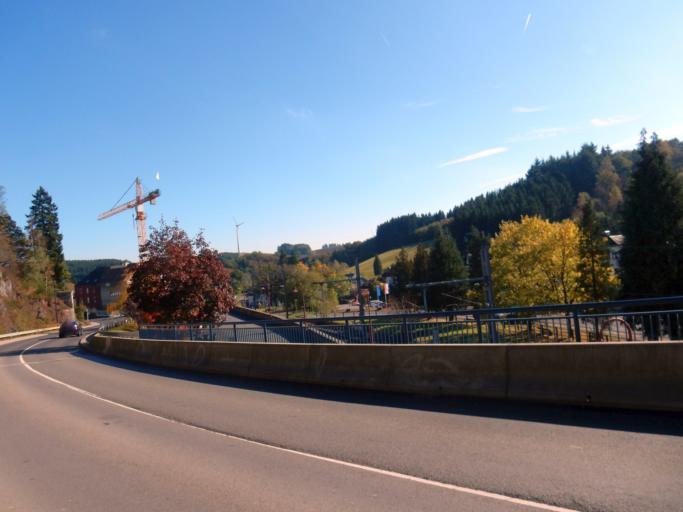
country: LU
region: Diekirch
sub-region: Canton de Clervaux
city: Troisvierges
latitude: 50.1186
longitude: 5.9933
